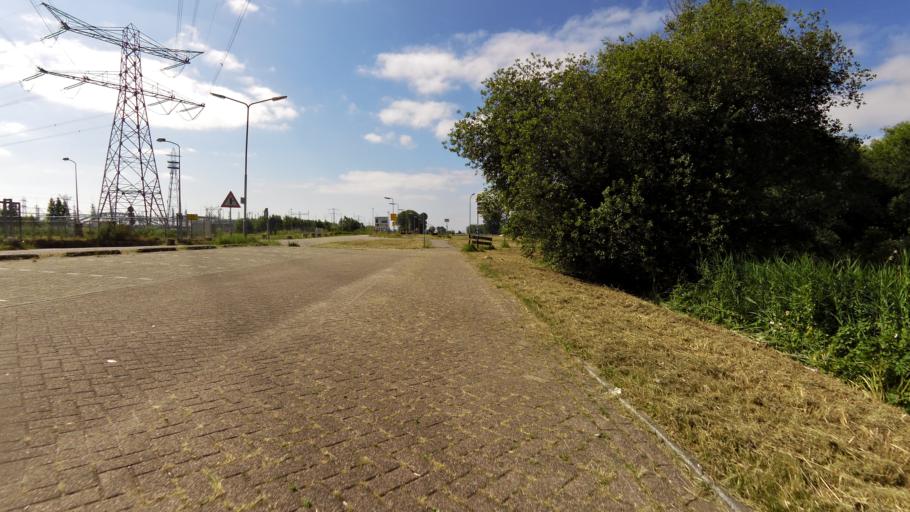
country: NL
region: North Holland
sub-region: Gemeente Amsterdam
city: Driemond
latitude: 52.3355
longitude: 5.0225
